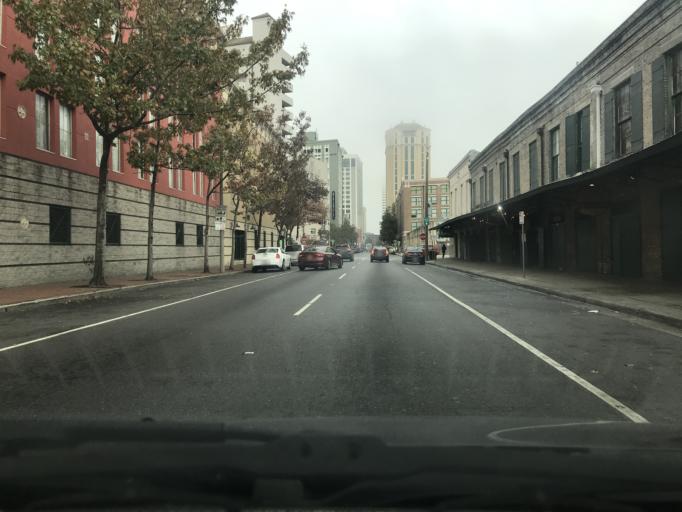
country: US
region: Louisiana
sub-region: Orleans Parish
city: New Orleans
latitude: 29.9439
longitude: -90.0658
